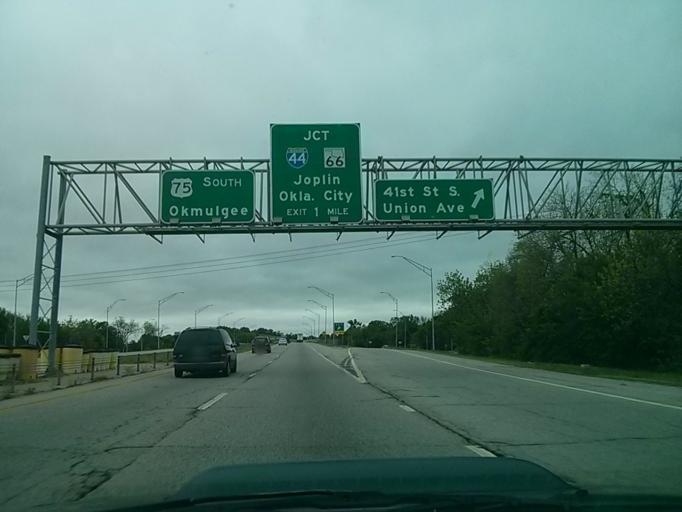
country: US
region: Oklahoma
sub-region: Tulsa County
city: Tulsa
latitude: 36.1072
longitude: -96.0106
